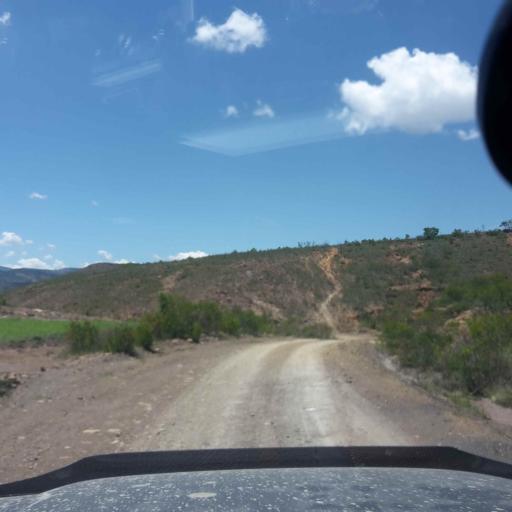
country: BO
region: Cochabamba
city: Totora
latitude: -17.7762
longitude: -65.2720
